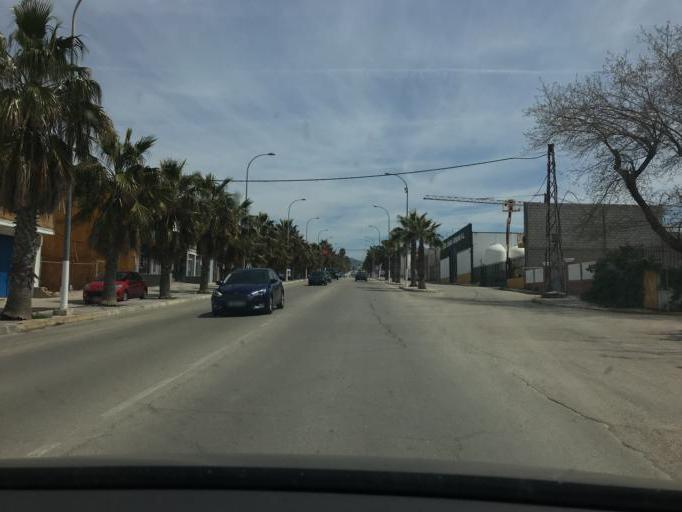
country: ES
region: Andalusia
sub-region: Provincia de Jaen
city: Torredonjimeno
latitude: 37.7631
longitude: -3.9428
